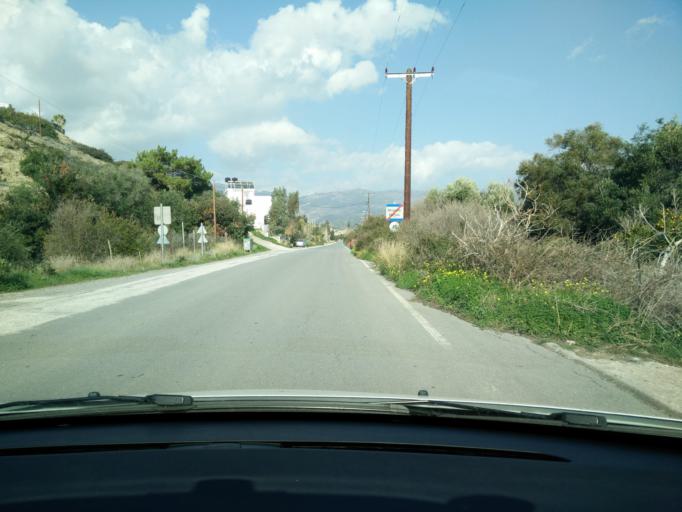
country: GR
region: Crete
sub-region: Nomos Lasithiou
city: Gra Liyia
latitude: 35.0071
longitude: 25.5837
